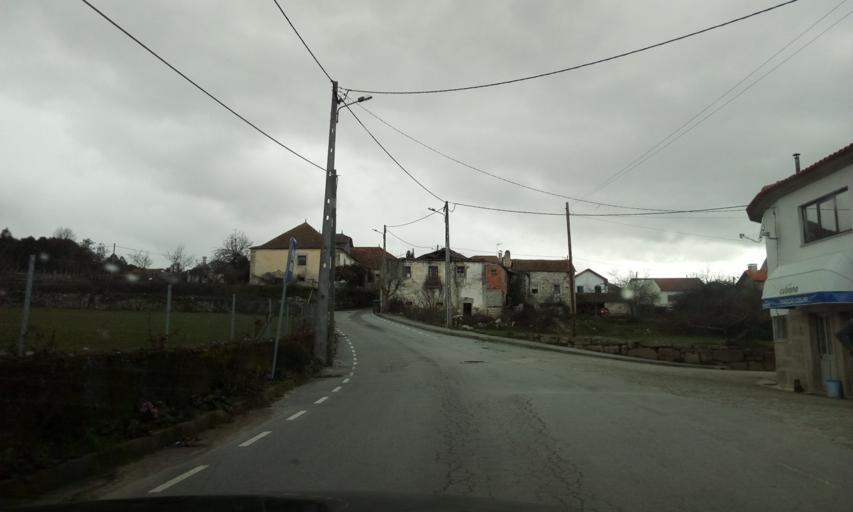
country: PT
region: Guarda
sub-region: Fornos de Algodres
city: Fornos de Algodres
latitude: 40.6391
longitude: -7.5970
